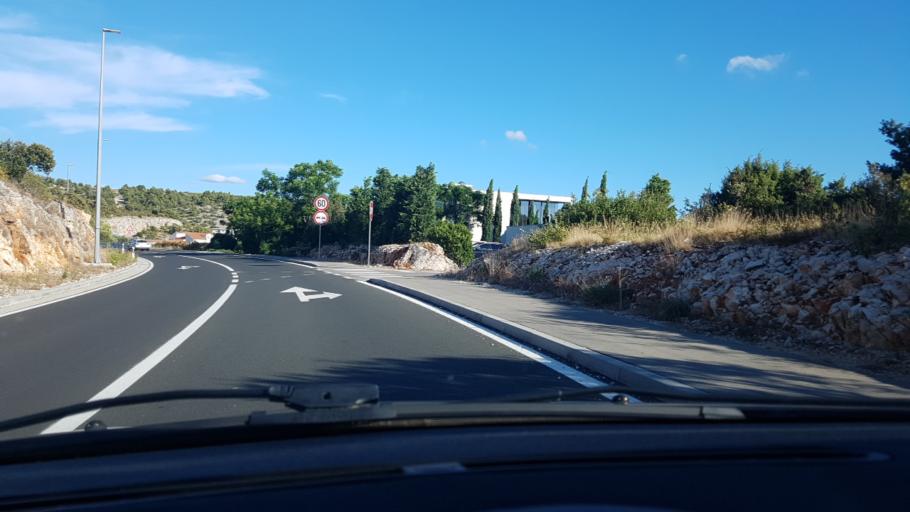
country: HR
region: Sibensko-Kniniska
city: Primosten
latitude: 43.6005
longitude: 15.9225
